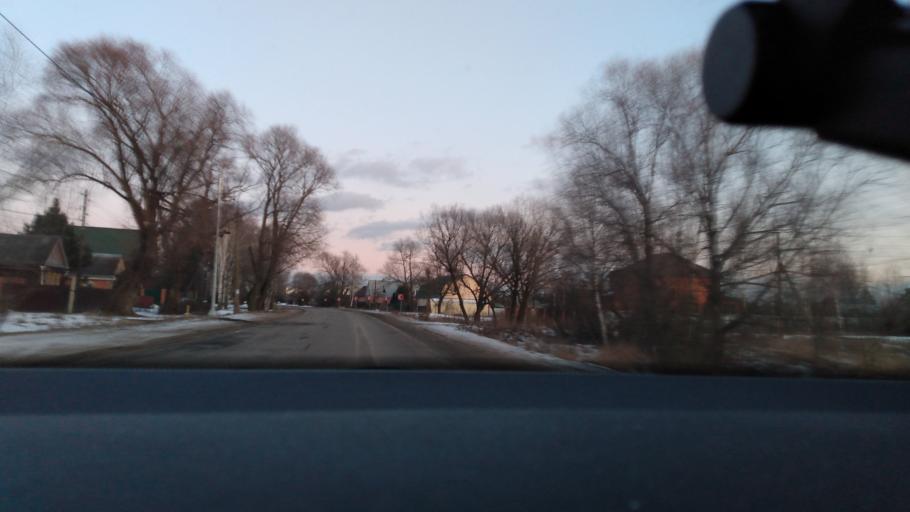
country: RU
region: Moskovskaya
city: Krasnaya Poyma
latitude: 55.1115
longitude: 39.0459
